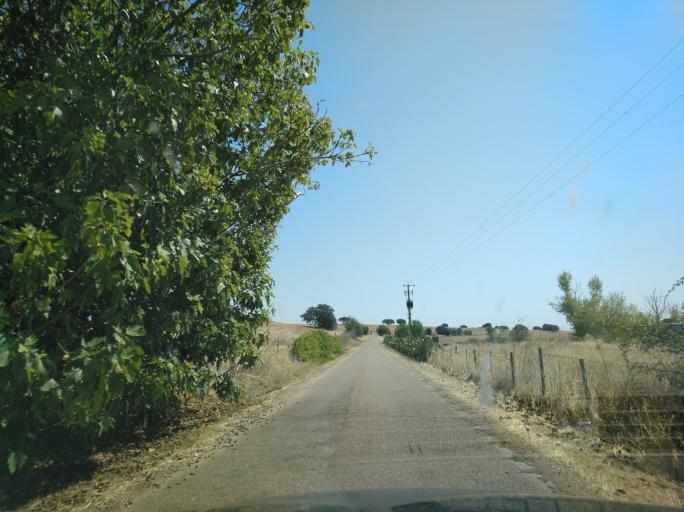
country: PT
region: Portalegre
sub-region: Campo Maior
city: Campo Maior
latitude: 39.0307
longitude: -7.0102
